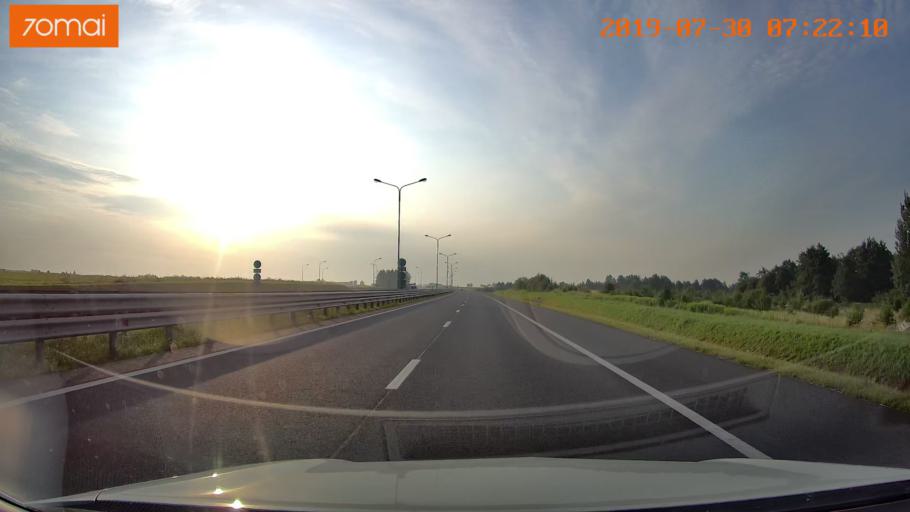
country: RU
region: Kaliningrad
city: Bol'shoe Isakovo
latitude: 54.6933
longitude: 20.7482
